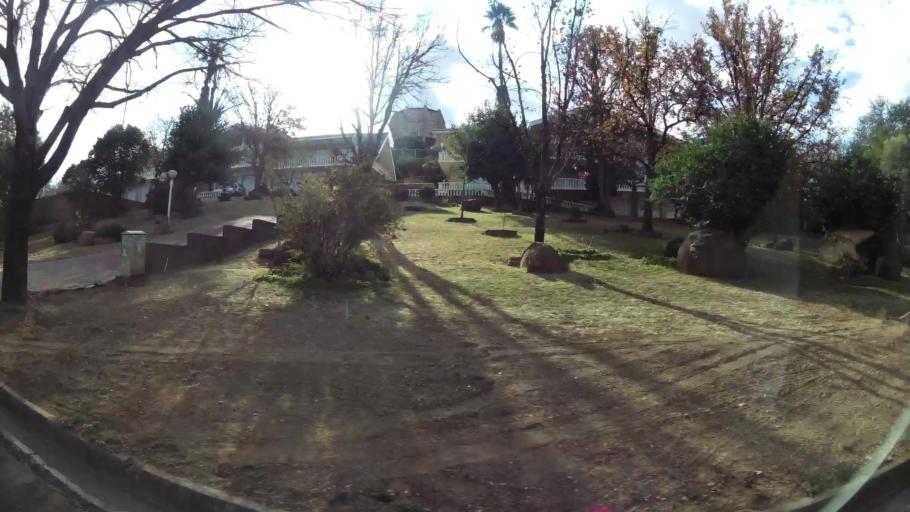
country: ZA
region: Orange Free State
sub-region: Mangaung Metropolitan Municipality
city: Bloemfontein
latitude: -29.0795
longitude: 26.2084
